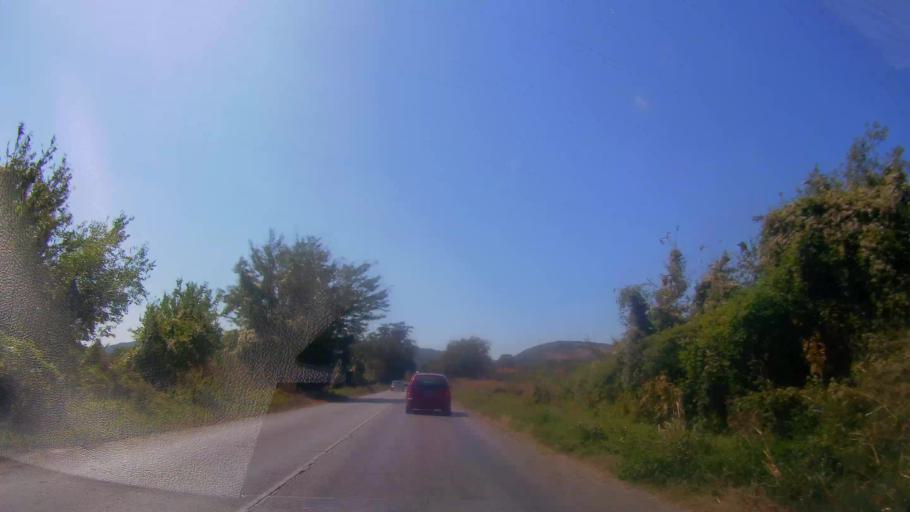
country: BG
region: Veliko Turnovo
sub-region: Obshtina Gorna Oryakhovitsa
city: Purvomaytsi
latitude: 43.1496
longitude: 25.6160
